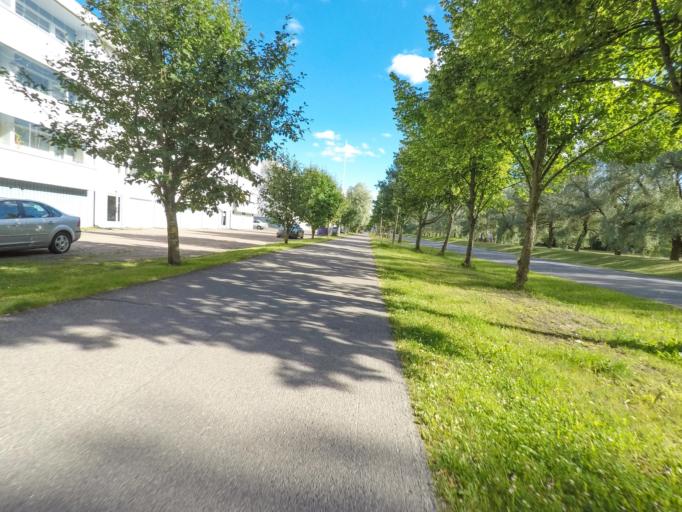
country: FI
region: South Karelia
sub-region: Lappeenranta
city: Lappeenranta
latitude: 61.0800
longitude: 28.1494
